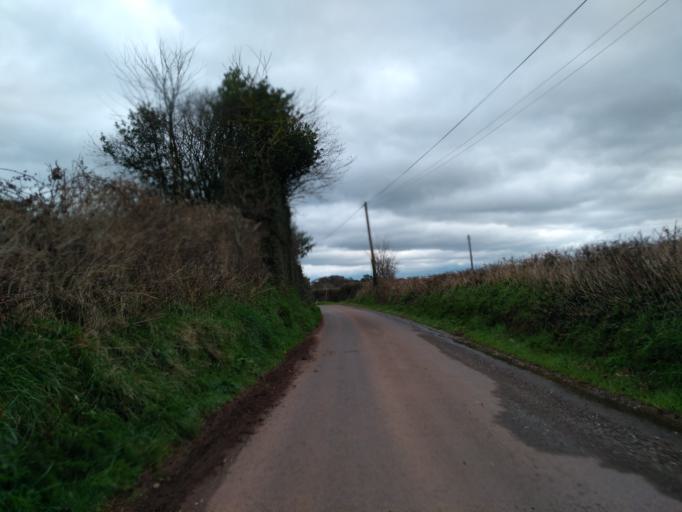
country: GB
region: England
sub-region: Devon
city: Exeter
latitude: 50.8062
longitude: -3.5443
